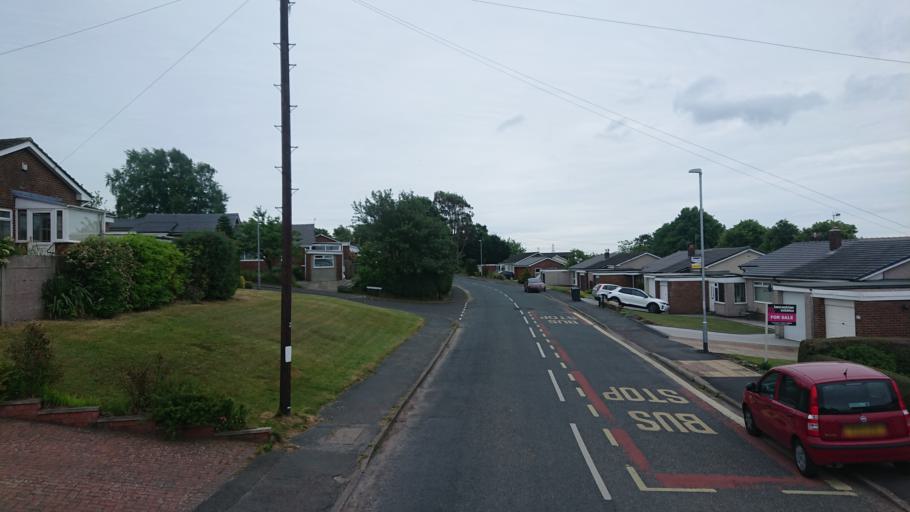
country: GB
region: England
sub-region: Lancashire
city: Lancaster
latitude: 54.0292
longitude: -2.7858
